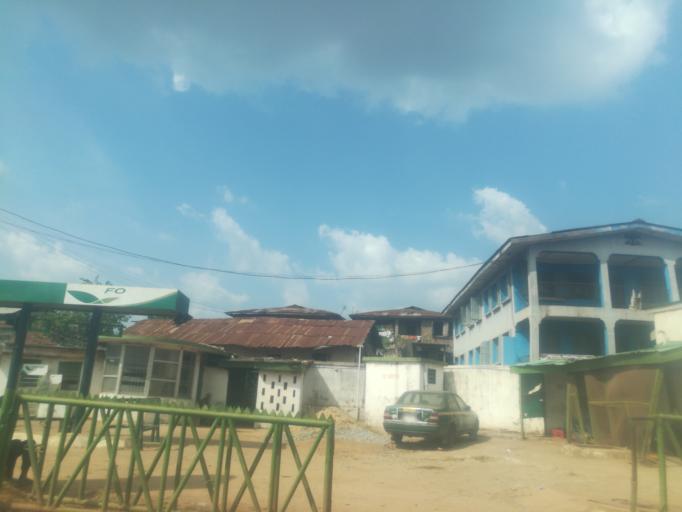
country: NG
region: Ogun
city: Abeokuta
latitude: 7.1696
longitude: 3.3608
